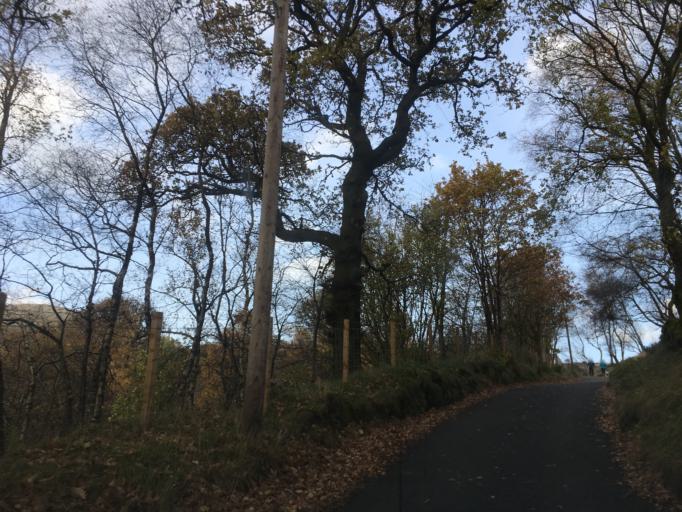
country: GB
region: Scotland
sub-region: Clackmannanshire
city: Dollar
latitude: 56.1736
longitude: -3.6725
